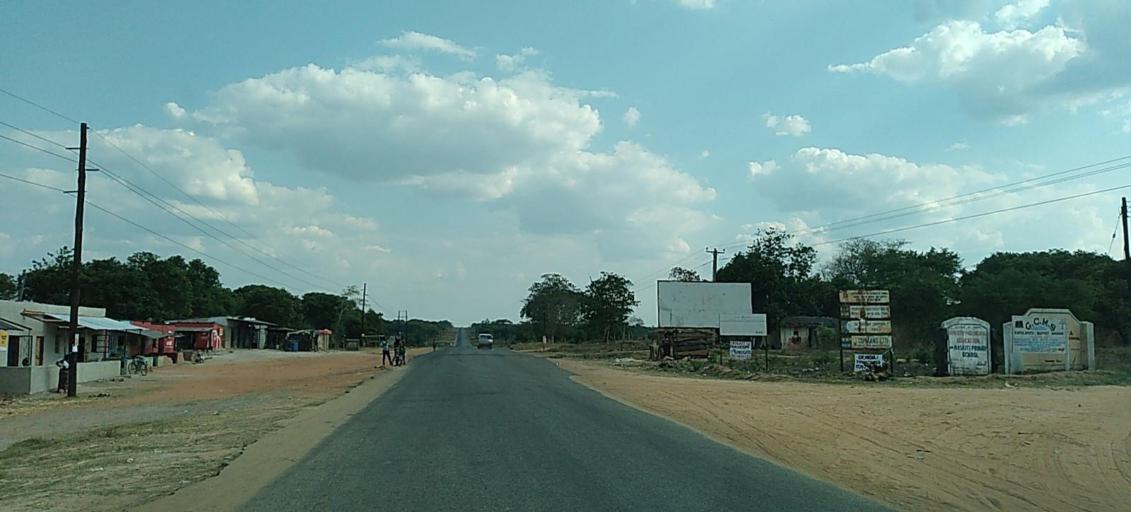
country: ZM
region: Copperbelt
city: Luanshya
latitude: -13.2612
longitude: 28.4064
